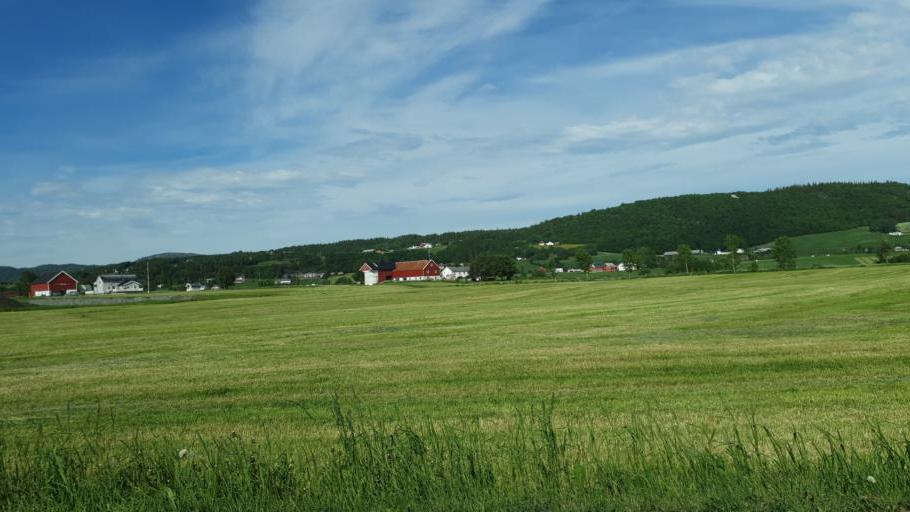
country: NO
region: Sor-Trondelag
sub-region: Rissa
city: Rissa
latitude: 63.4971
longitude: 10.0123
